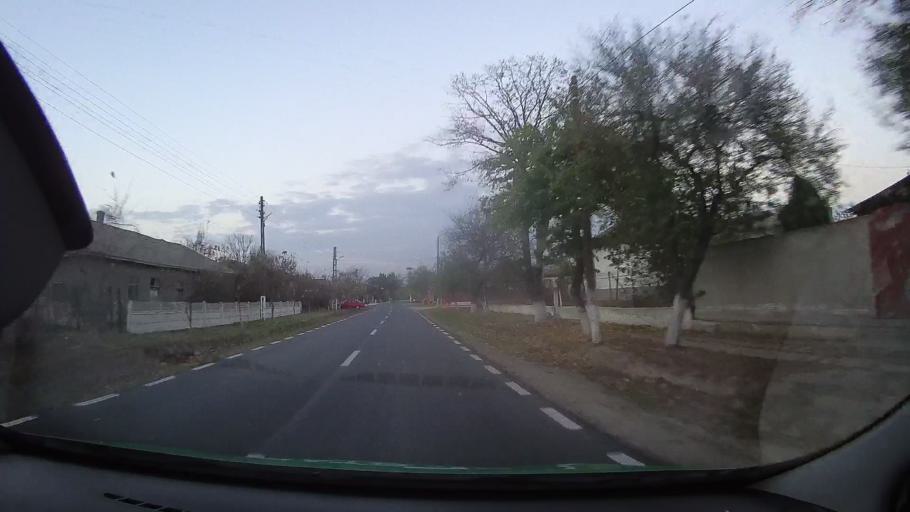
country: RO
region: Constanta
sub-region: Comuna Oltina
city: Oltina
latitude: 44.1608
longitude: 27.6675
